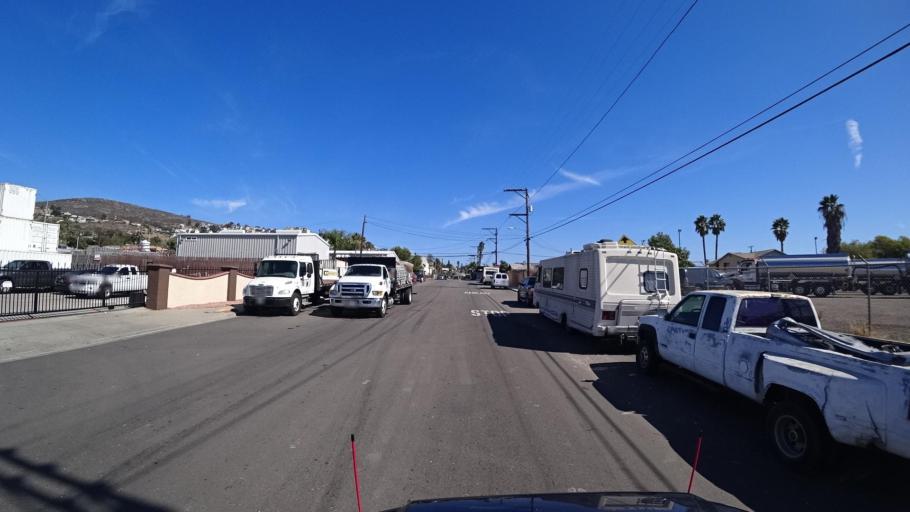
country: US
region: California
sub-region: San Diego County
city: La Presa
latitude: 32.7167
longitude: -117.0025
